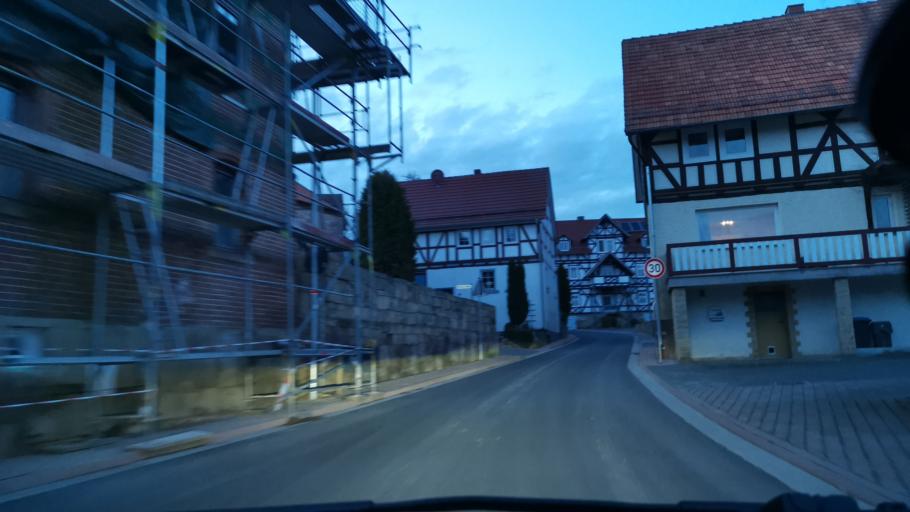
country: DE
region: Hesse
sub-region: Regierungsbezirk Kassel
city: Cornberg
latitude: 51.0680
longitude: 9.8201
